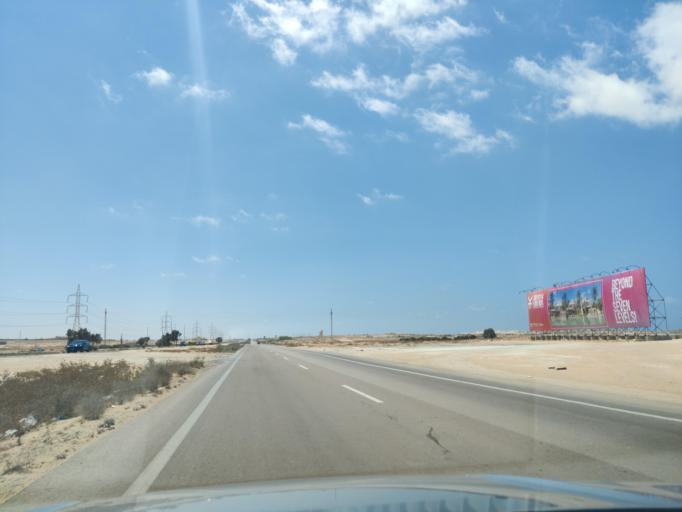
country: EG
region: Muhafazat Matruh
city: Al `Alamayn
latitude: 31.0656
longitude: 28.1852
